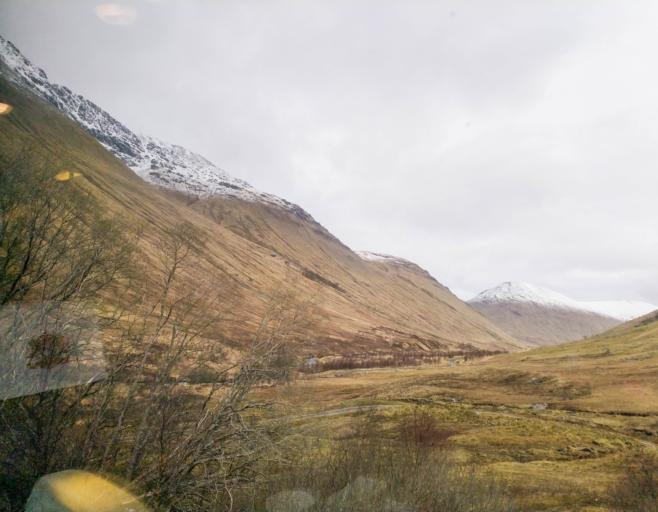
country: GB
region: Scotland
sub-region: Argyll and Bute
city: Garelochhead
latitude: 56.4883
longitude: -4.7037
